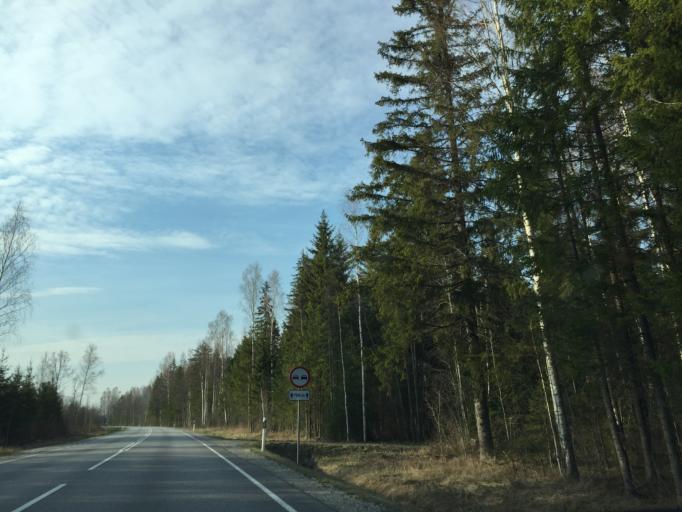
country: EE
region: Jogevamaa
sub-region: Mustvee linn
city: Mustvee
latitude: 58.8580
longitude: 26.8555
